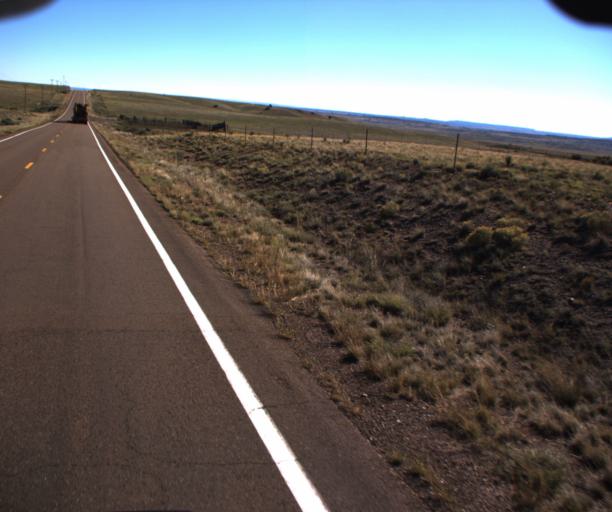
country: US
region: Arizona
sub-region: Apache County
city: Saint Johns
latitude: 34.5034
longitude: -109.4849
